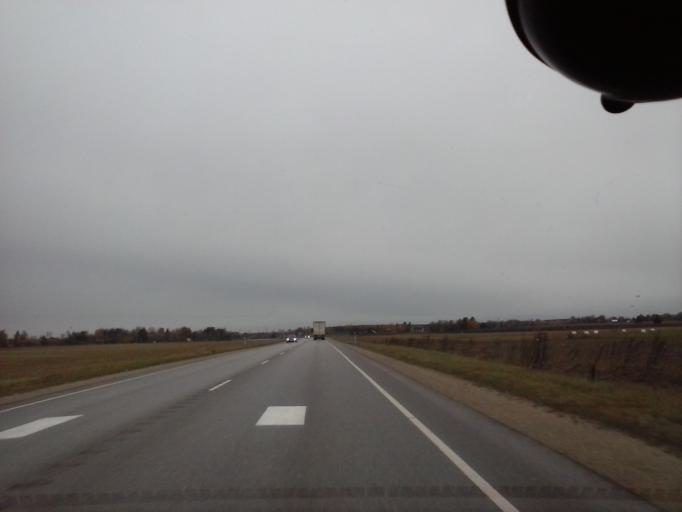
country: EE
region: Jogevamaa
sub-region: Poltsamaa linn
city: Poltsamaa
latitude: 58.6683
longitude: 25.9738
